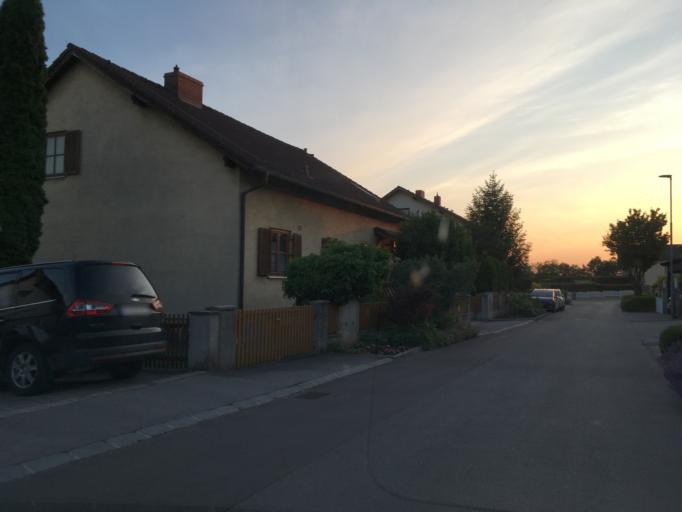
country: AT
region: Lower Austria
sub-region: Politischer Bezirk Korneuburg
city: Stockerau
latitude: 48.3916
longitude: 16.1962
